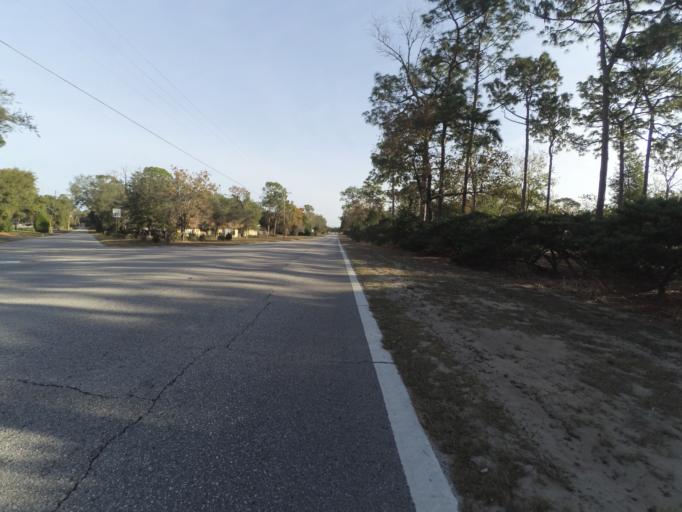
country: US
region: Florida
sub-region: Lake County
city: Umatilla
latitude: 28.9396
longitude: -81.6380
